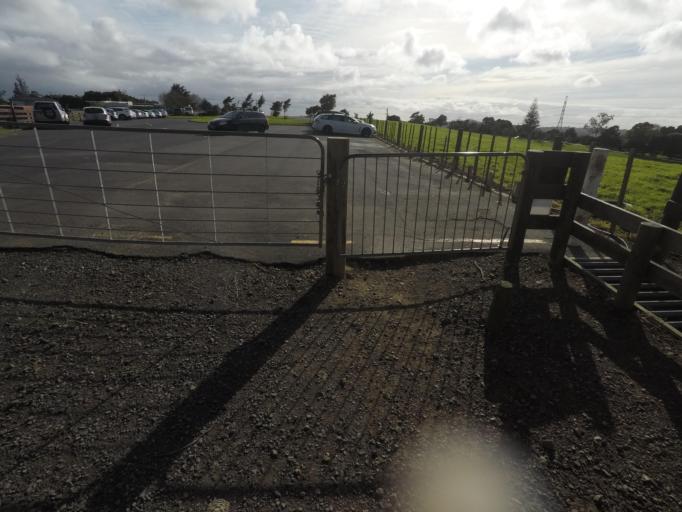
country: NZ
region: Auckland
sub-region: Auckland
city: Manukau City
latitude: -36.9905
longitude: 174.9045
